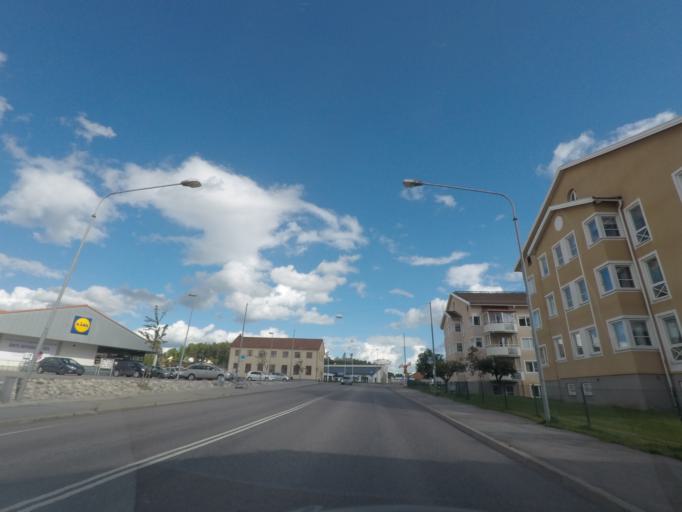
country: SE
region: OErebro
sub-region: Lindesbergs Kommun
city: Lindesberg
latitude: 59.5978
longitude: 15.2238
